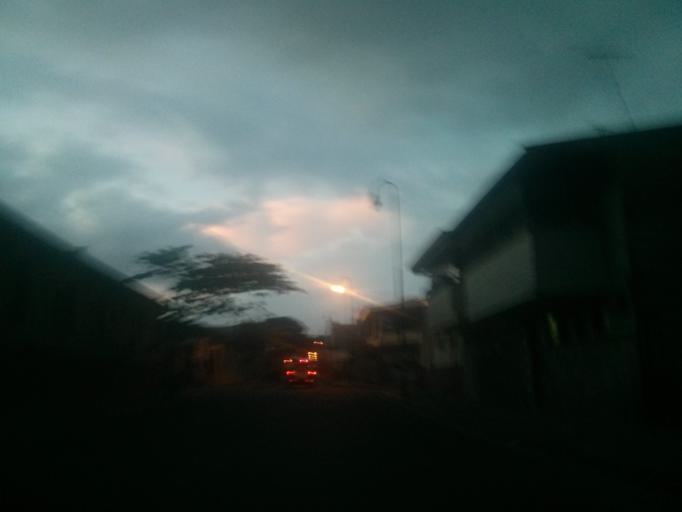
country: CR
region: San Jose
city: San Jose
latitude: 9.9267
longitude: -84.0775
